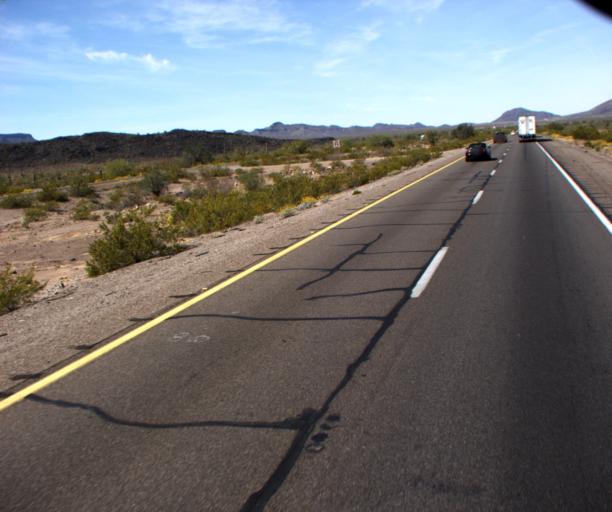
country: US
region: Arizona
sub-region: La Paz County
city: Quartzsite
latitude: 33.6541
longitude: -113.9448
